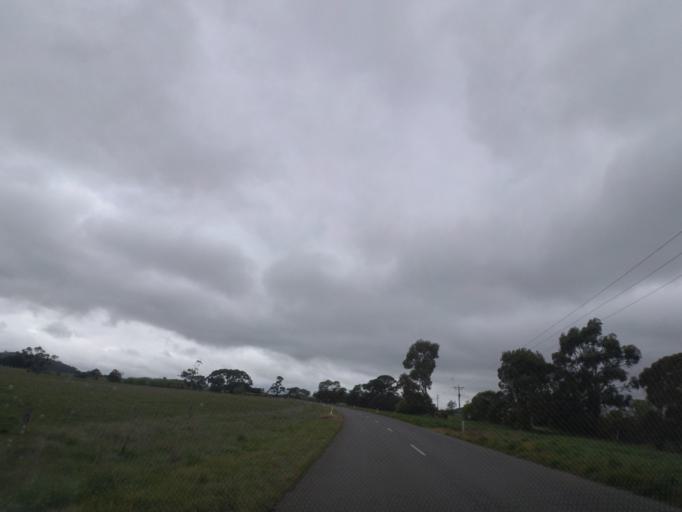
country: AU
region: Victoria
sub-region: Hume
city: Sunbury
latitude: -37.3250
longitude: 144.5579
